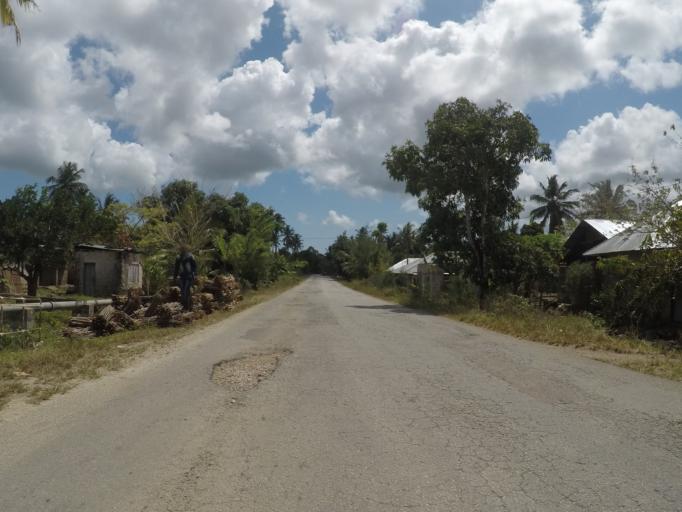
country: TZ
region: Zanzibar Central/South
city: Nganane
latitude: -6.2883
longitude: 39.4411
